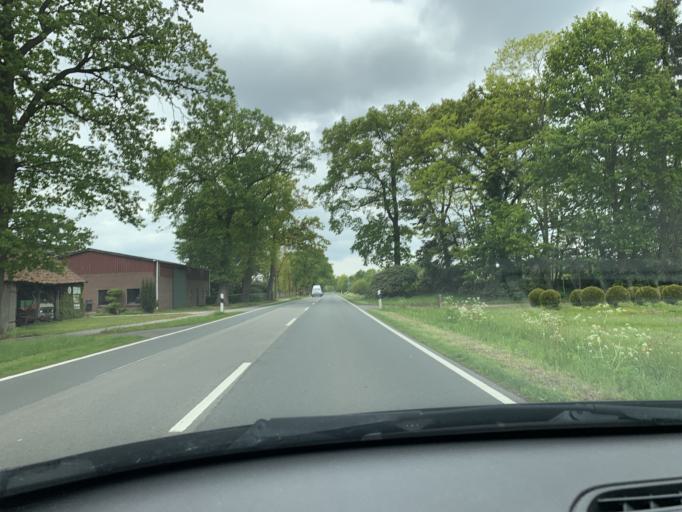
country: DE
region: Lower Saxony
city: Bad Zwischenahn
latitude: 53.1848
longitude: 8.0631
